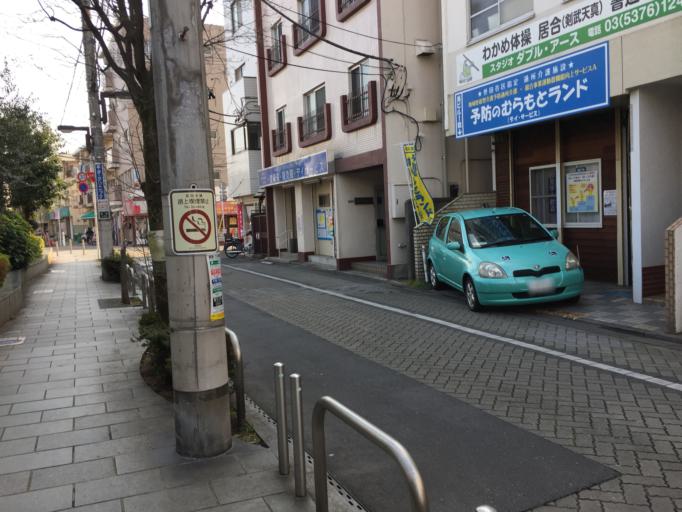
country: JP
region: Tokyo
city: Tokyo
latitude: 35.6601
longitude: 139.6419
